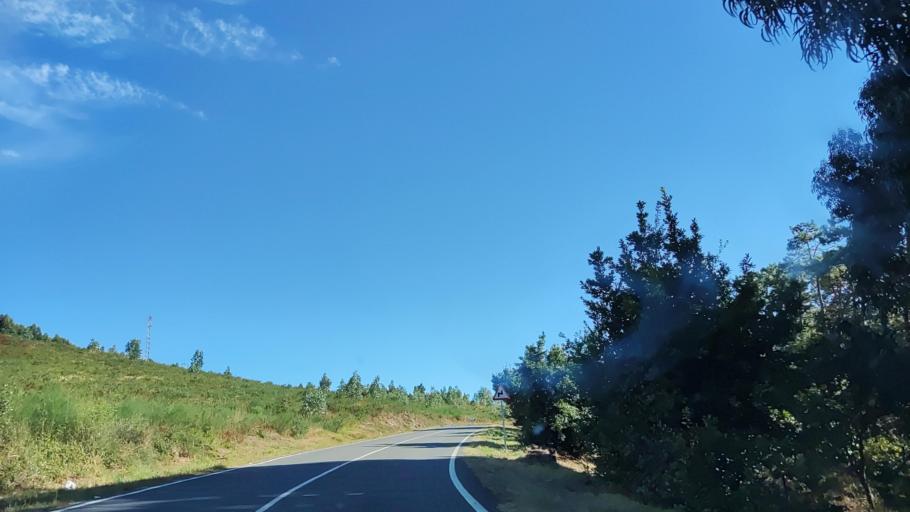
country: ES
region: Galicia
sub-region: Provincia da Coruna
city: Boiro
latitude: 42.5592
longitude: -9.0221
